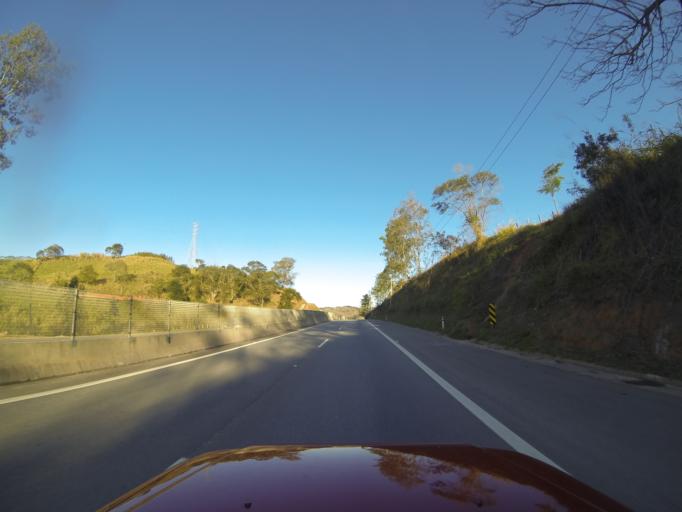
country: BR
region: Sao Paulo
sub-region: Santa Branca
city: Santa Branca
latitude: -23.3195
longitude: -45.7475
